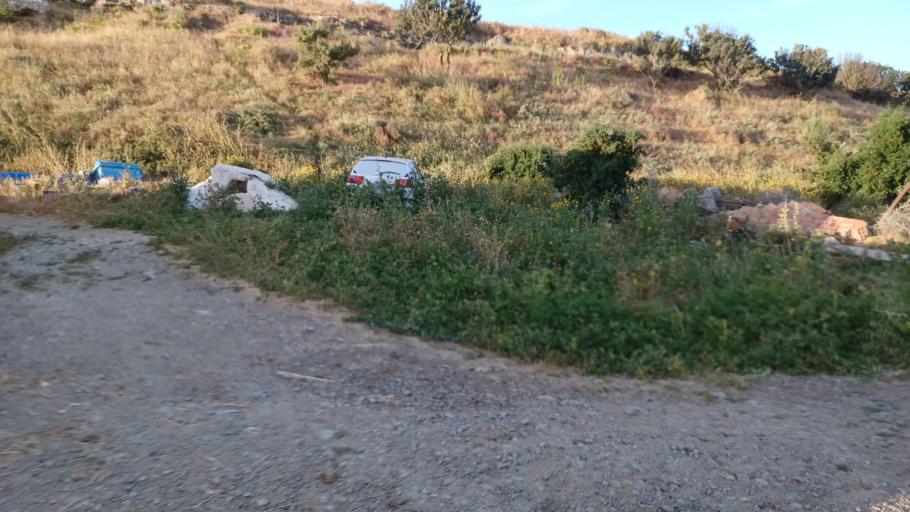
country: CY
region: Lefkosia
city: Kokkinotrimithia
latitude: 35.1713
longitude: 33.1579
